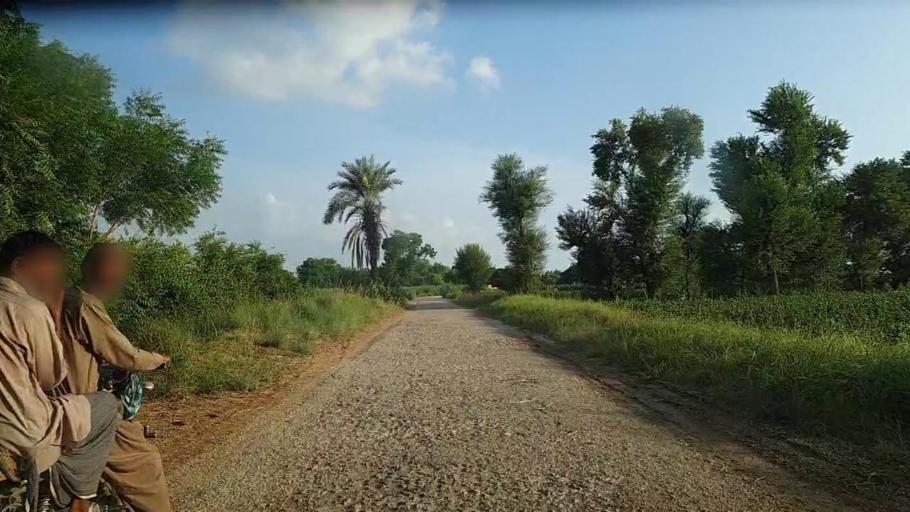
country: PK
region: Sindh
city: Hingorja
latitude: 27.0622
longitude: 68.4188
